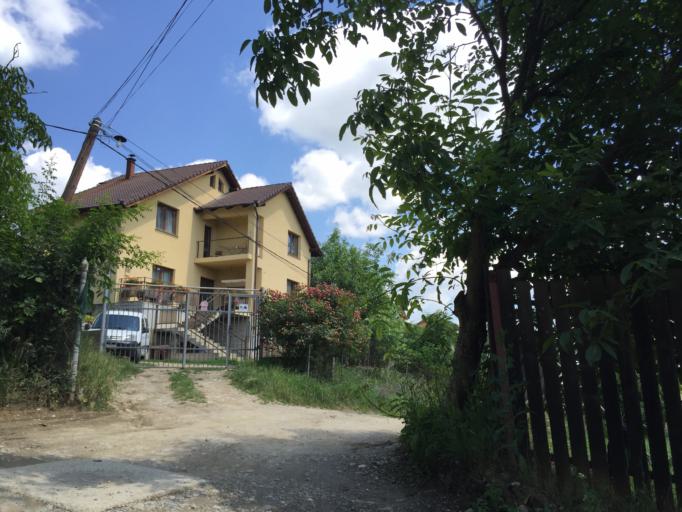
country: RO
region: Cluj
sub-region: Municipiul Cluj-Napoca
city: Cluj-Napoca
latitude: 46.7971
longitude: 23.5938
